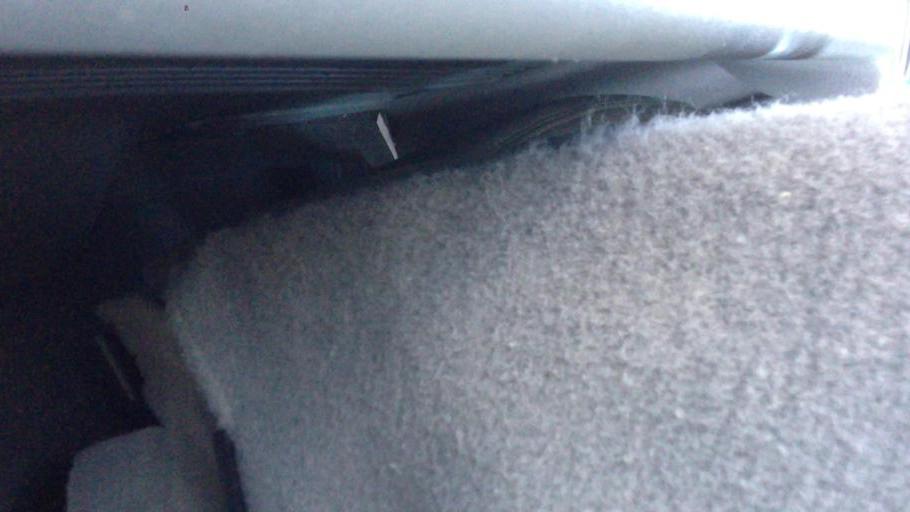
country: US
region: New York
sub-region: Dutchess County
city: Tivoli
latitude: 42.1146
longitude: -73.8187
